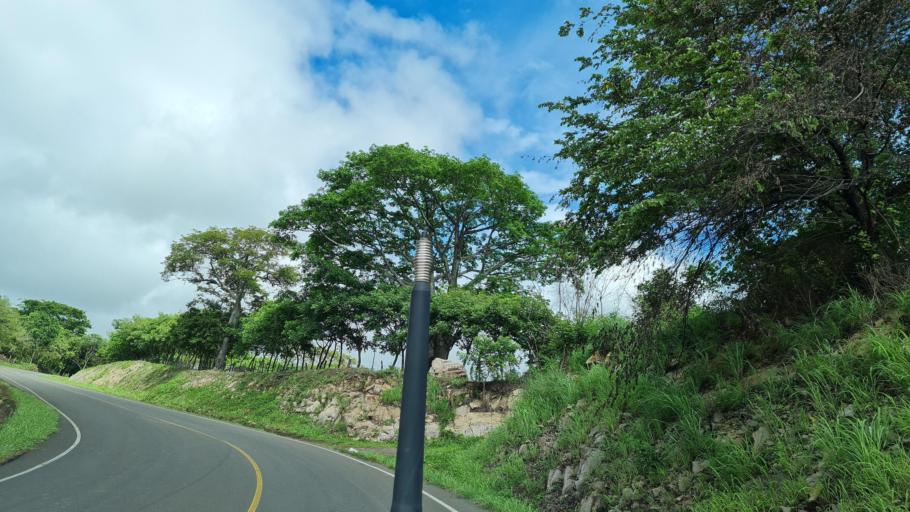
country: NI
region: Boaco
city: San Jose de los Remates
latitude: 12.6121
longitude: -85.8912
